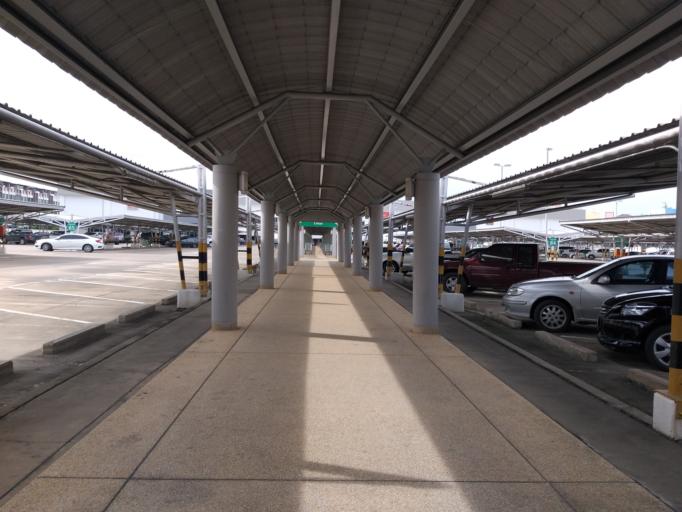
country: TH
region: Pathum Thani
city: Thanyaburi
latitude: 13.9998
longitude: 100.6811
